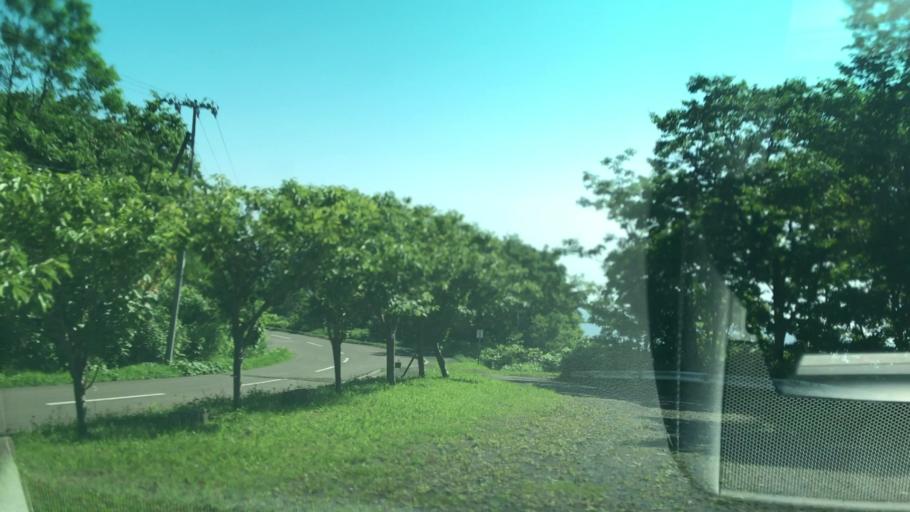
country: JP
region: Hokkaido
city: Iwanai
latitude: 43.1506
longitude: 140.4186
